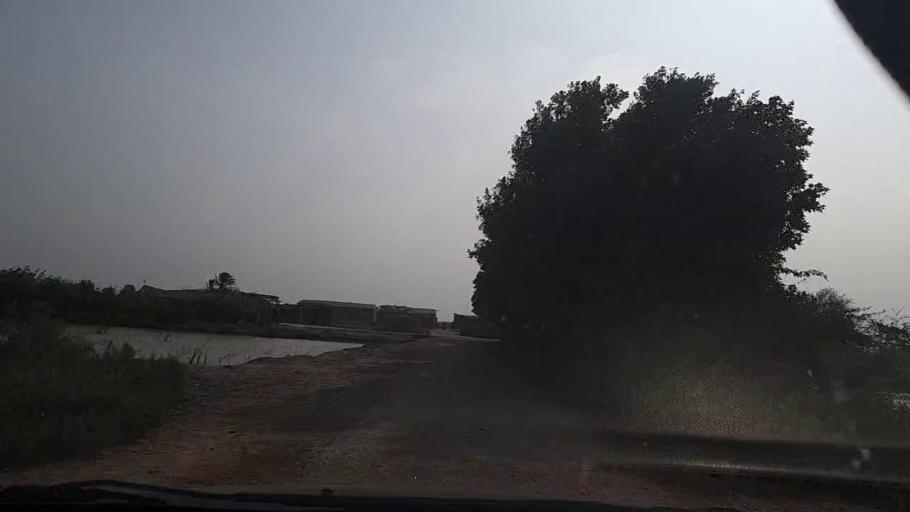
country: PK
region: Sindh
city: Thatta
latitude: 24.6131
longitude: 67.9461
